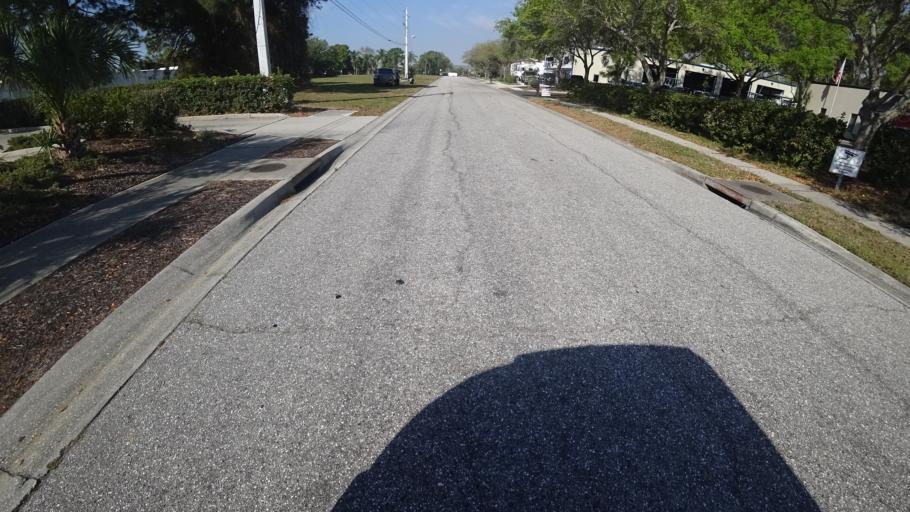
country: US
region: Florida
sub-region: Manatee County
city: Whitfield
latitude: 27.4083
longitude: -82.5535
